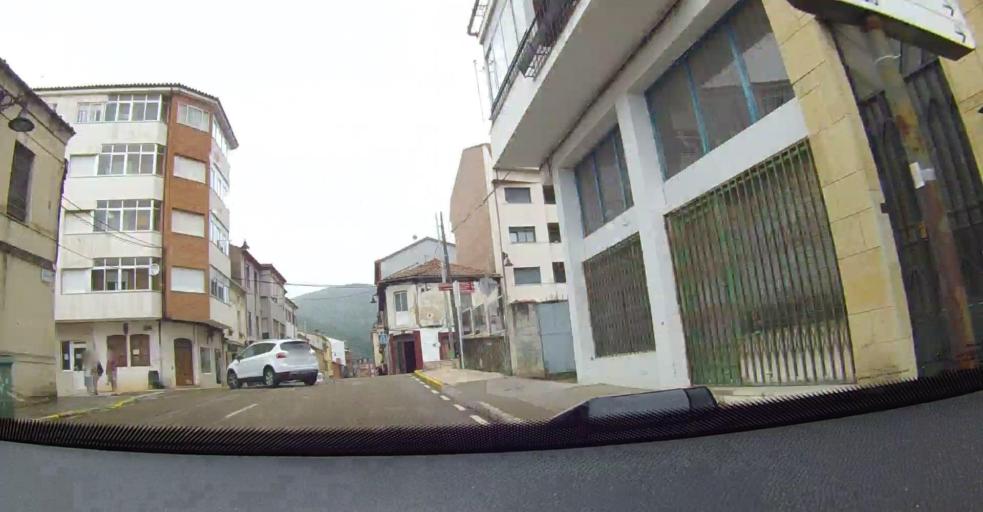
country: ES
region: Castille and Leon
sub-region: Provincia de Leon
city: Cistierna
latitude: 42.8018
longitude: -5.1264
